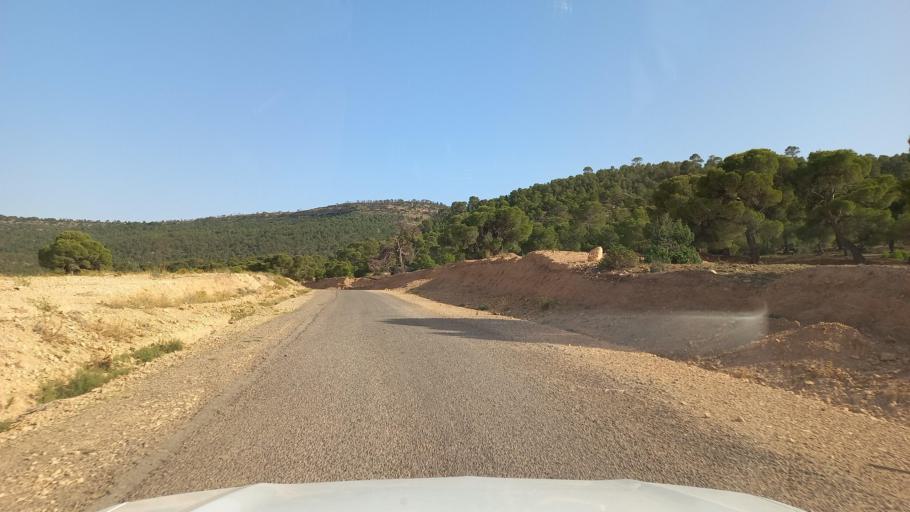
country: TN
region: Al Qasrayn
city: Kasserine
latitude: 35.3342
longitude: 8.8407
